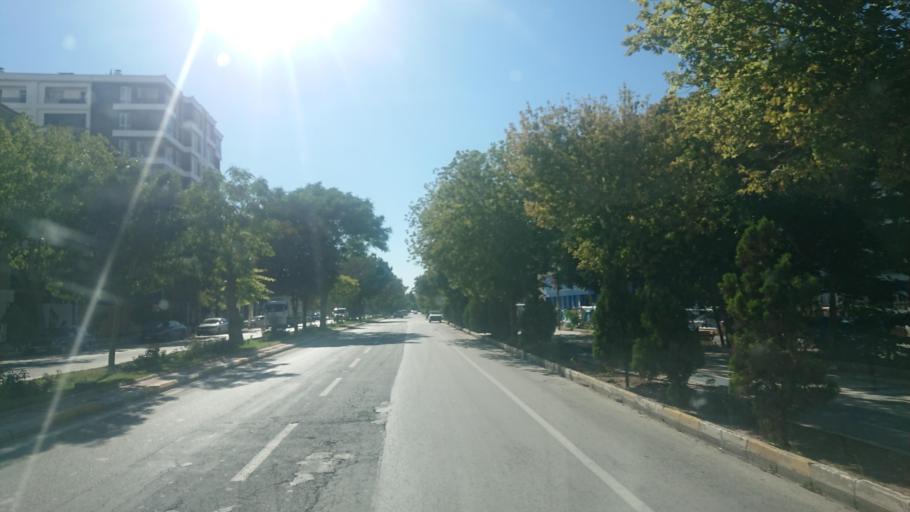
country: TR
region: Aksaray
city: Aksaray
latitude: 38.3642
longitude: 34.0155
